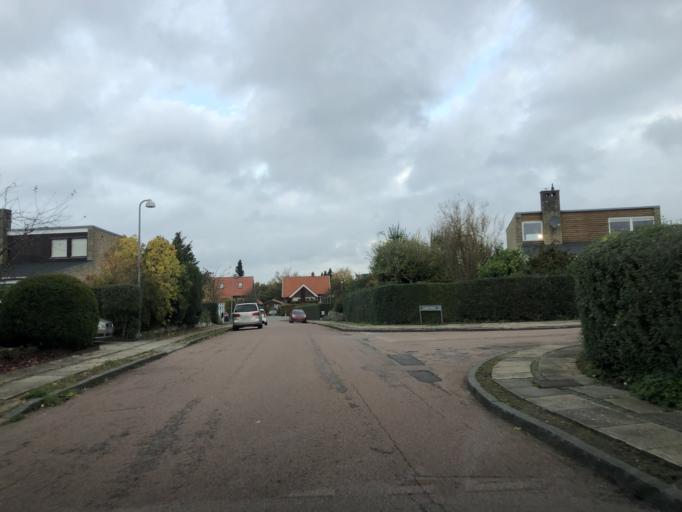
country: DK
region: Capital Region
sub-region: Rudersdal Kommune
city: Holte
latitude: 55.7905
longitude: 12.4666
